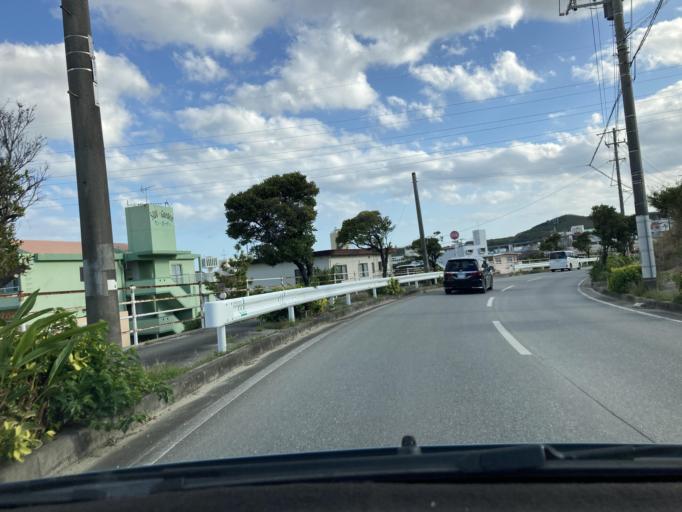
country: JP
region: Okinawa
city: Tomigusuku
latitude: 26.1873
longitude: 127.7073
